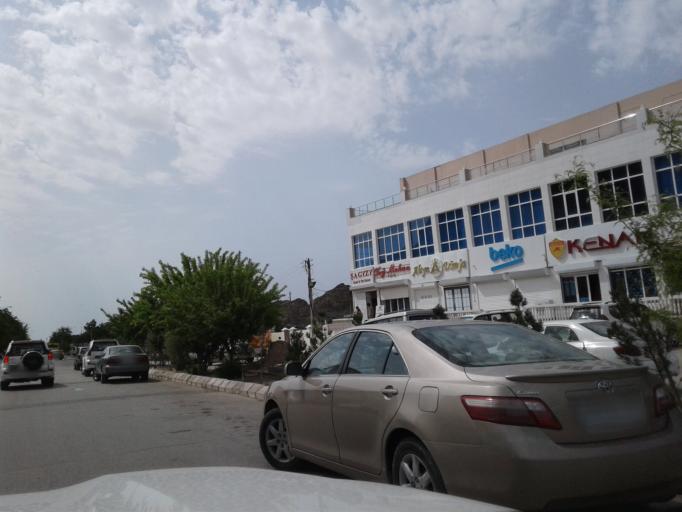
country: TM
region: Balkan
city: Turkmenbasy
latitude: 39.9983
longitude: 52.9699
